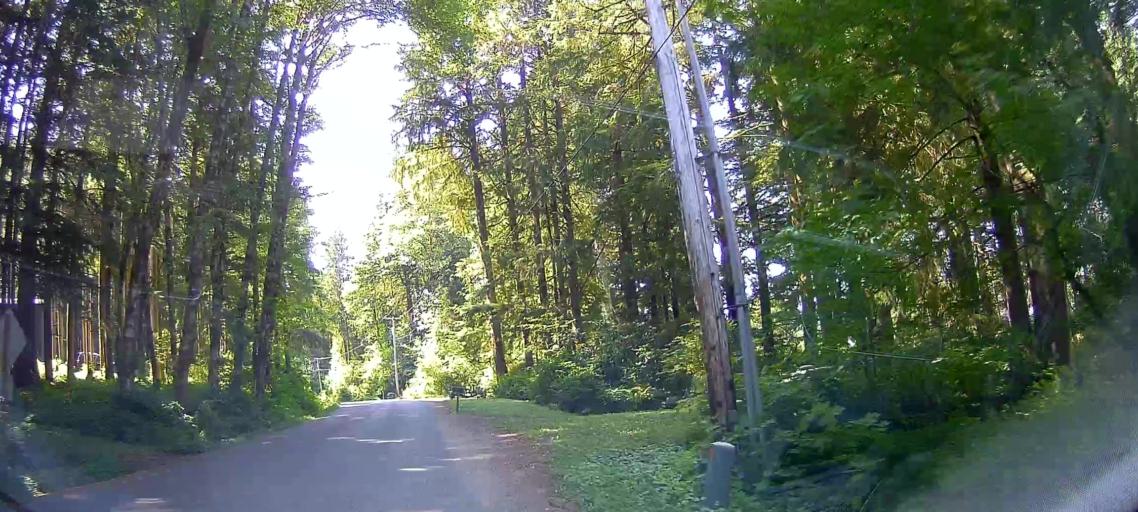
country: US
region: Washington
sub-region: Snohomish County
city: Arlington Heights
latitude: 48.3178
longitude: -122.0221
